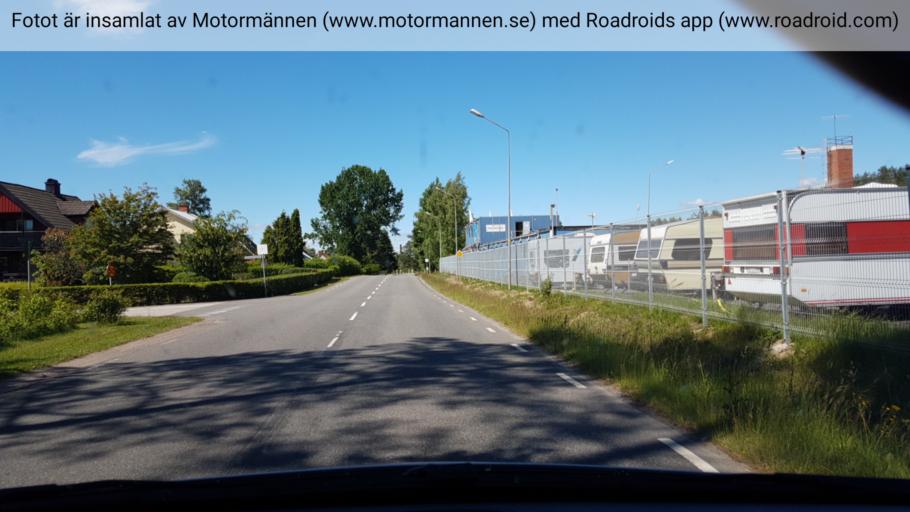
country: SE
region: Vaestra Goetaland
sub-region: Gullspangs Kommun
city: Hova
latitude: 58.8434
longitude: 14.2248
